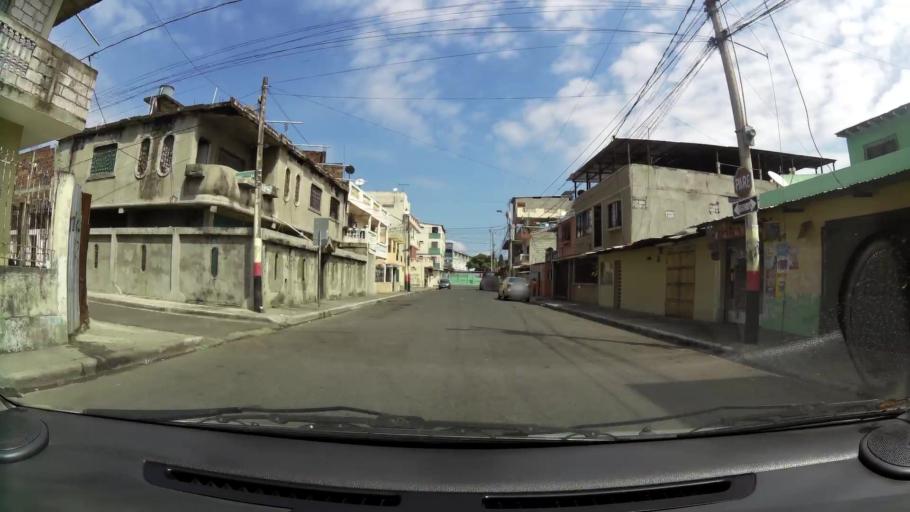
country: EC
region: Guayas
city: Guayaquil
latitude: -2.2545
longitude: -79.8929
